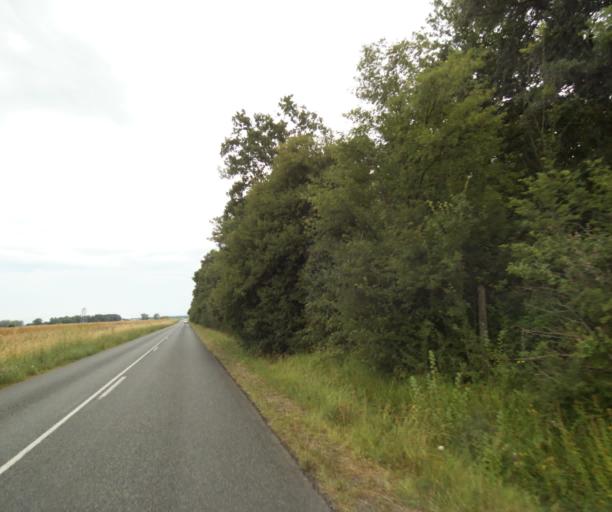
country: FR
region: Ile-de-France
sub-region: Departement de Seine-et-Marne
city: Saint-Sauveur-sur-Ecole
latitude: 48.5119
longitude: 2.5367
